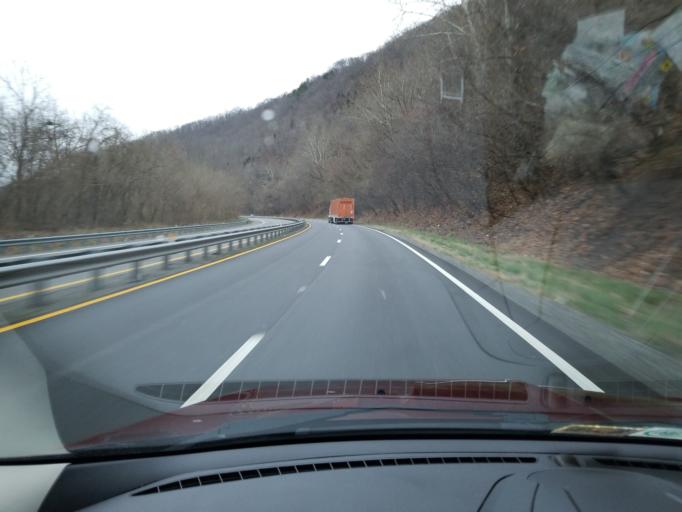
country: US
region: Virginia
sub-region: Giles County
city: Narrows
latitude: 37.3890
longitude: -80.8350
